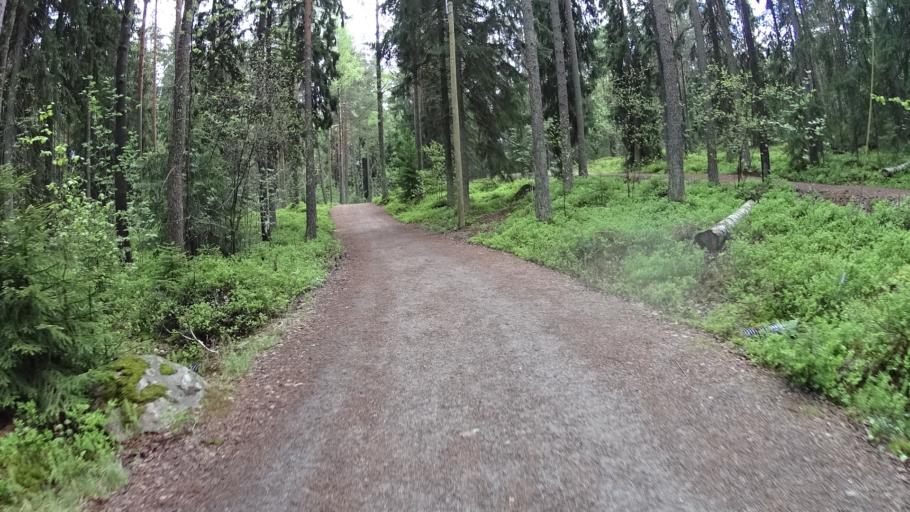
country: FI
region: Uusimaa
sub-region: Helsinki
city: Espoo
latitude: 60.2133
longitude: 24.6865
